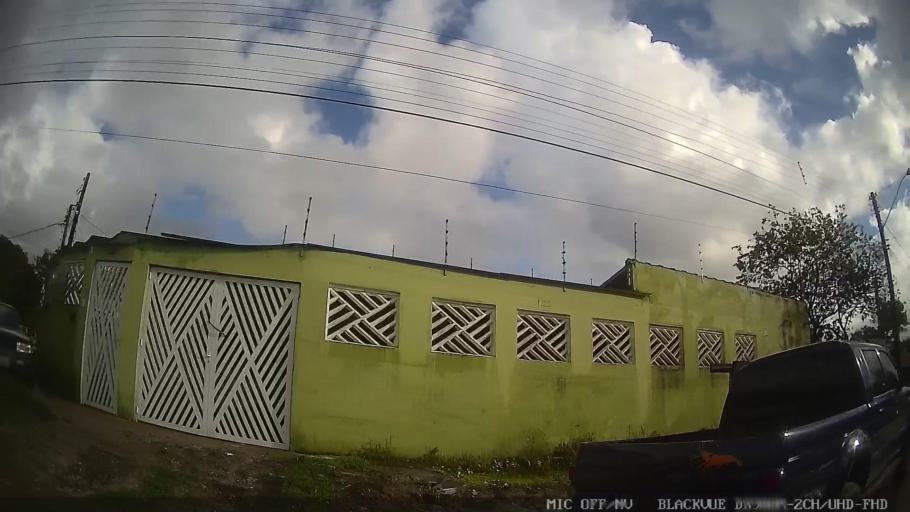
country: BR
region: Sao Paulo
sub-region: Itanhaem
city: Itanhaem
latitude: -24.1747
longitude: -46.8498
